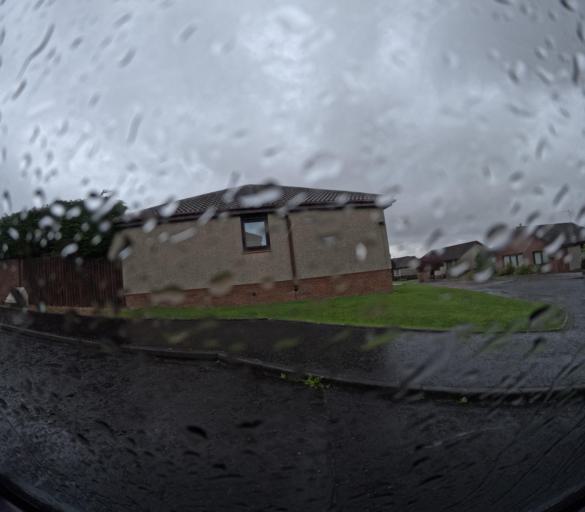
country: GB
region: Scotland
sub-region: West Lothian
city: West Calder
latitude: 55.8755
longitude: -3.5911
